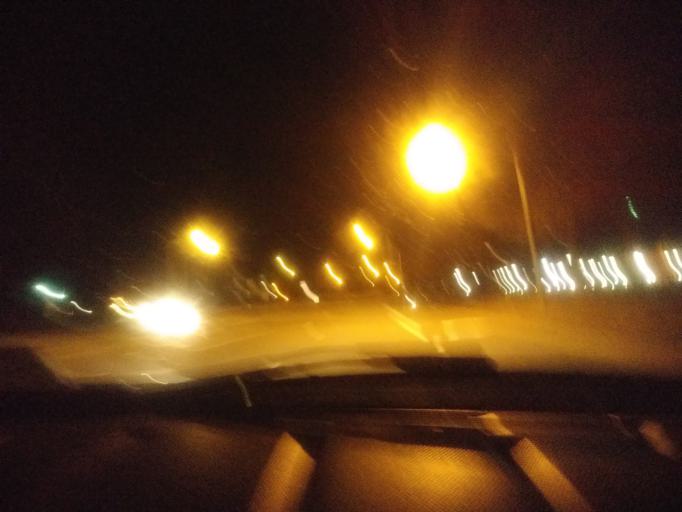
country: US
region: Virginia
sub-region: City of Chesapeake
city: Chesapeake
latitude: 36.8018
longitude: -76.1881
